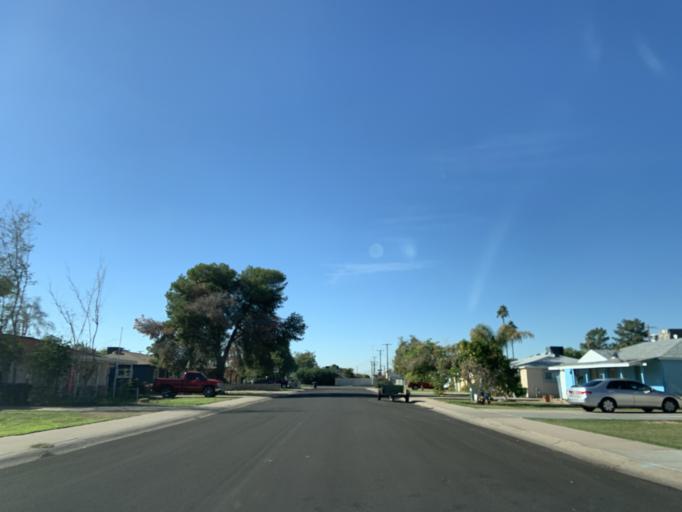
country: US
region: Arizona
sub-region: Maricopa County
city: Mesa
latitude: 33.4172
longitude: -111.8642
